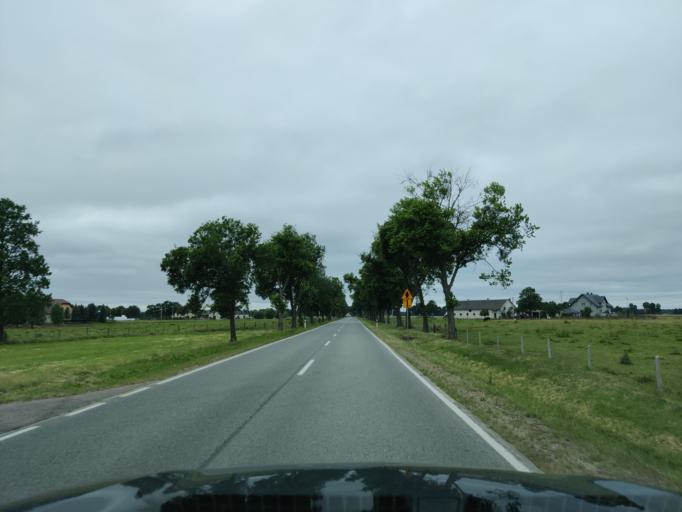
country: PL
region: Masovian Voivodeship
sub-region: Powiat ostrolecki
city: Czarnia
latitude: 53.3248
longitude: 21.1520
